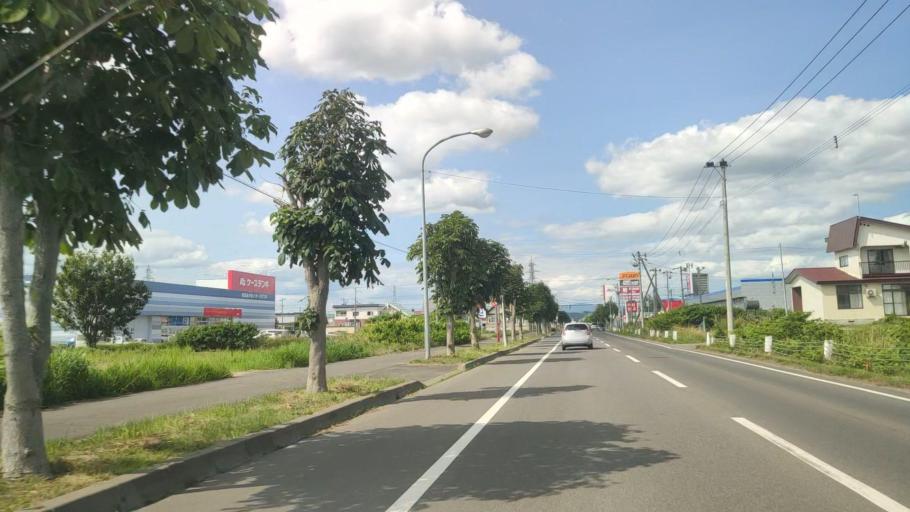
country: JP
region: Hokkaido
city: Nayoro
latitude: 44.3350
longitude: 142.4503
